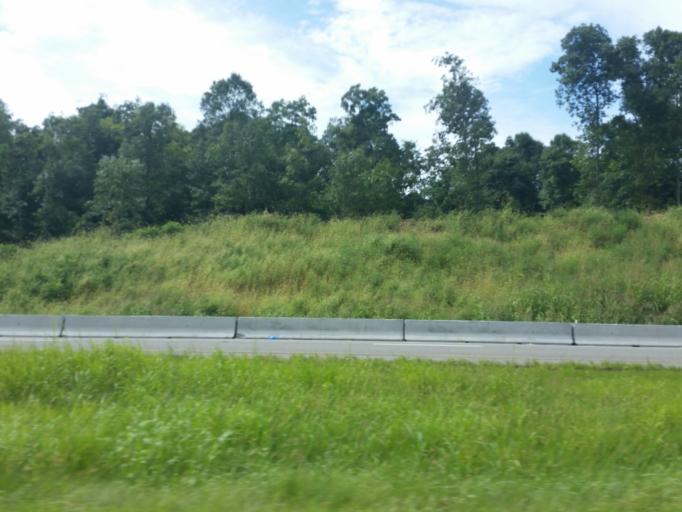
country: US
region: Kentucky
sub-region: Marshall County
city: Calvert City
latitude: 36.9950
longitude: -88.3319
